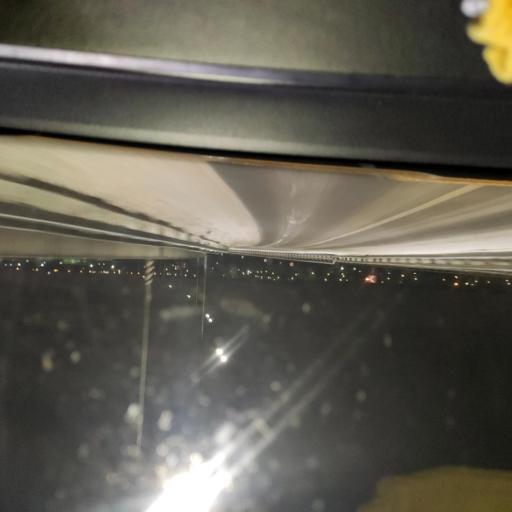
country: RU
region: Moskovskaya
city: Kokoshkino
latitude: 55.5918
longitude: 37.1506
